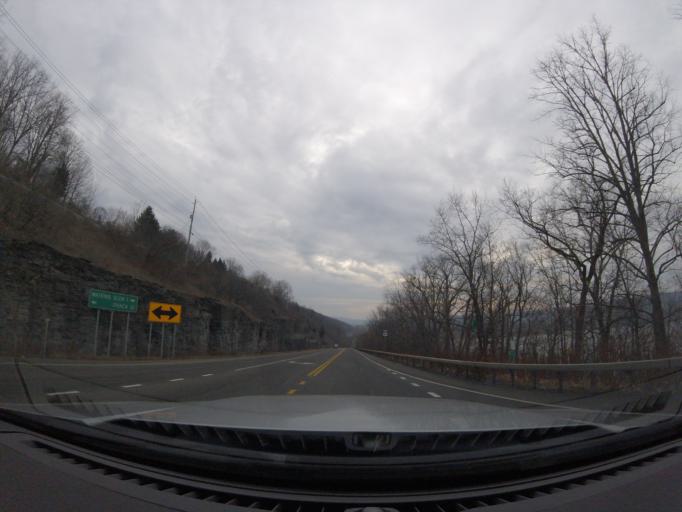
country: US
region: New York
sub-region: Schuyler County
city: Watkins Glen
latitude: 42.3949
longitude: -76.8570
